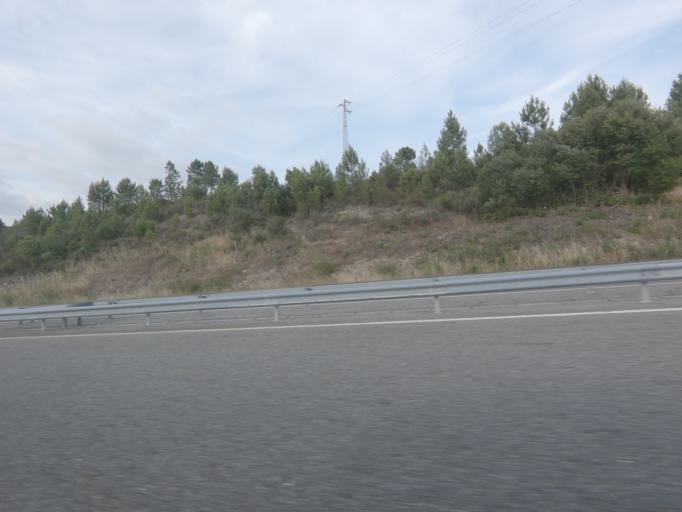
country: PT
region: Vila Real
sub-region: Boticas
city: Boticas
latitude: 41.6307
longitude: -7.5957
